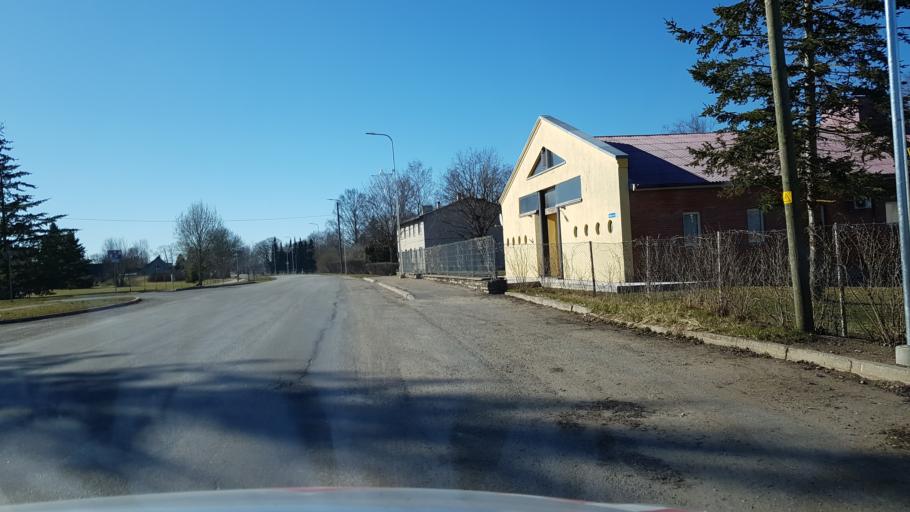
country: EE
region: Laeaene-Virumaa
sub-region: Haljala vald
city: Haljala
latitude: 59.4329
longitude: 26.2644
